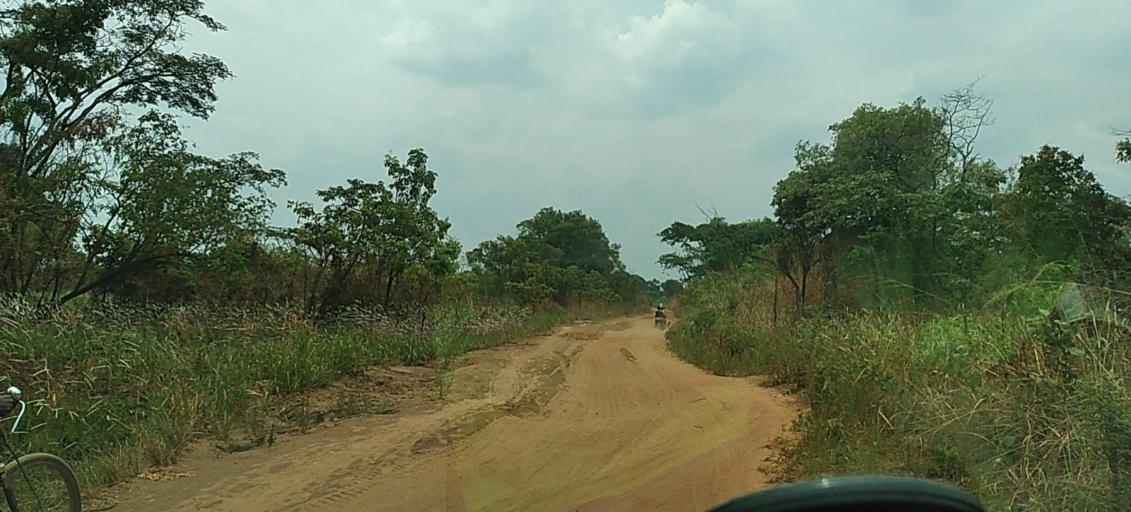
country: ZM
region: North-Western
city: Kansanshi
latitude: -12.0703
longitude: 26.3539
